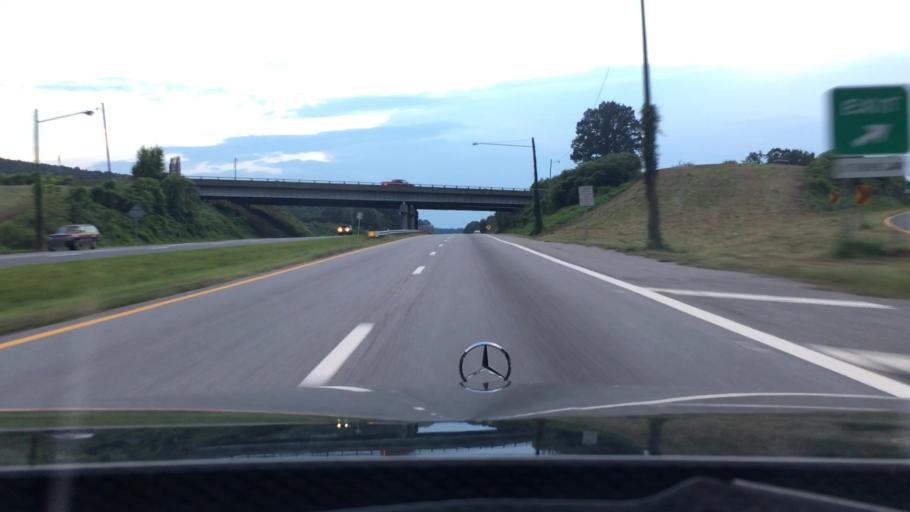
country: US
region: Virginia
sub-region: City of Lynchburg
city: Lynchburg
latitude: 37.3788
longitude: -79.1285
